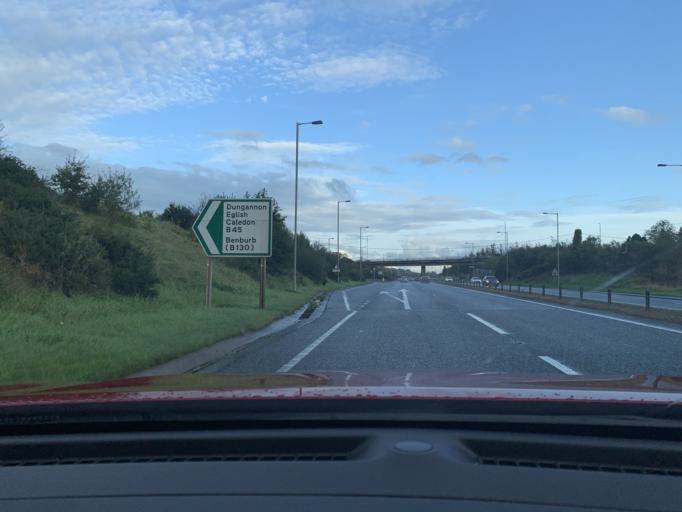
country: GB
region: Northern Ireland
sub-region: Dungannon District
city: Dungannon
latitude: 54.4816
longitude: -6.7920
